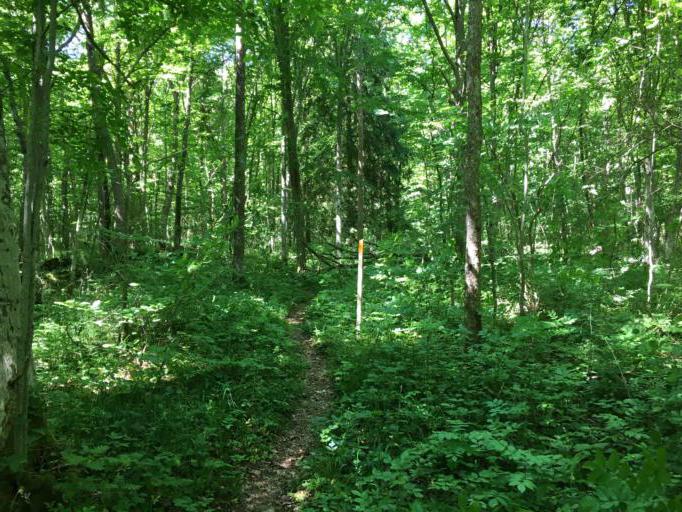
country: SE
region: Kalmar
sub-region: Borgholms Kommun
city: Borgholm
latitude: 56.7509
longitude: 16.6051
